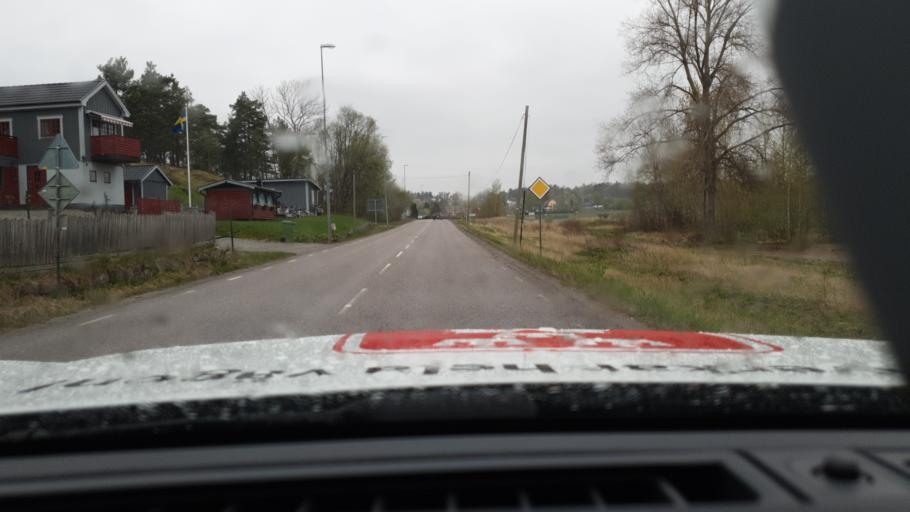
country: SE
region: Soedermanland
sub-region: Strangnas Kommun
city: Mariefred
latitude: 59.2614
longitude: 17.2138
